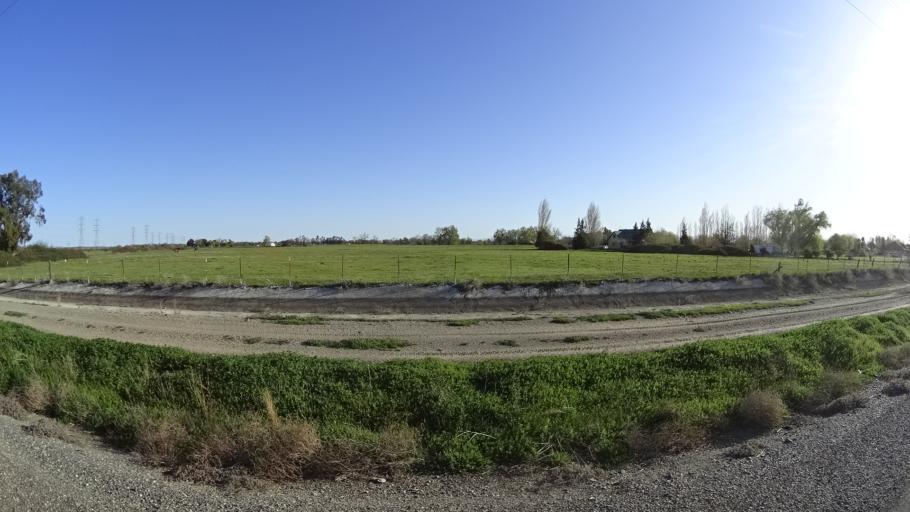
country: US
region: California
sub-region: Glenn County
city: Orland
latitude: 39.7719
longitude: -122.2634
